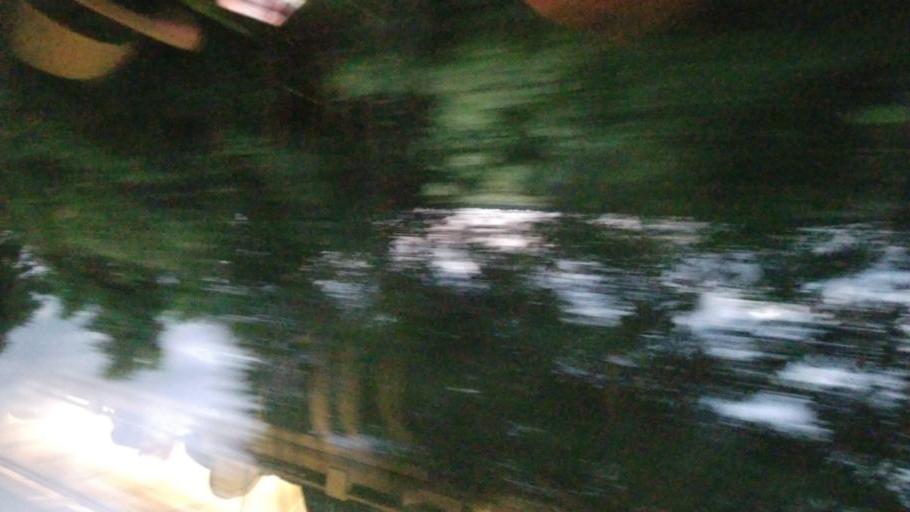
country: US
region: Virginia
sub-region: Orange County
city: Gordonsville
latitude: 38.2156
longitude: -78.2077
